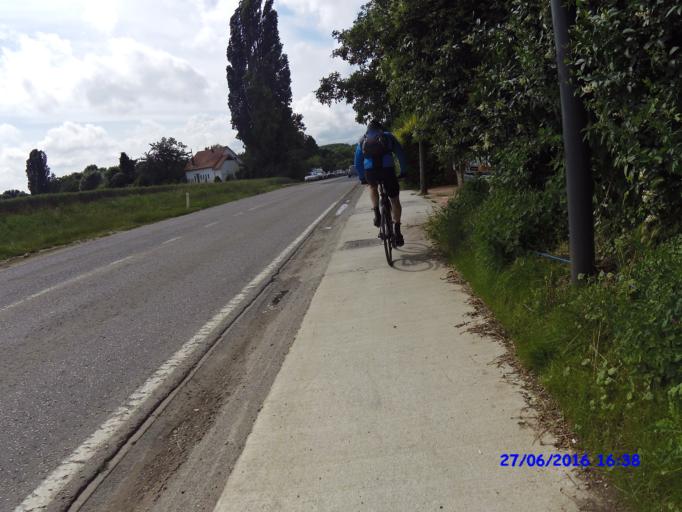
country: BE
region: Flanders
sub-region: Provincie Vlaams-Brabant
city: Dilbeek
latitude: 50.8166
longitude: 4.2590
